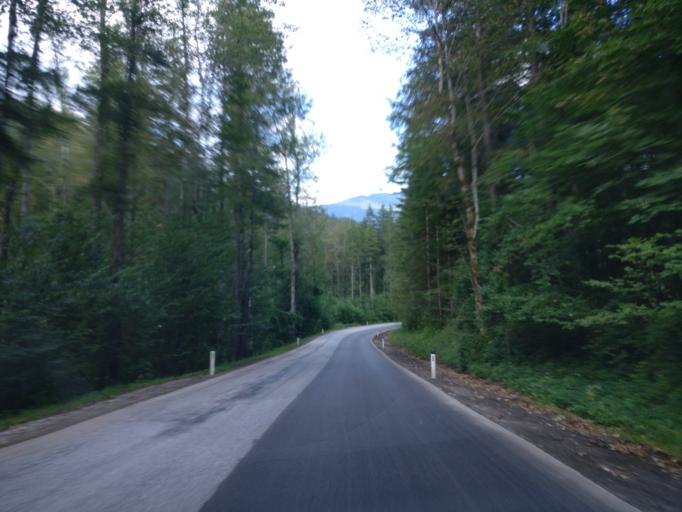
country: AT
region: Styria
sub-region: Politischer Bezirk Liezen
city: Johnsbach
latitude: 47.5884
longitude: 14.6227
